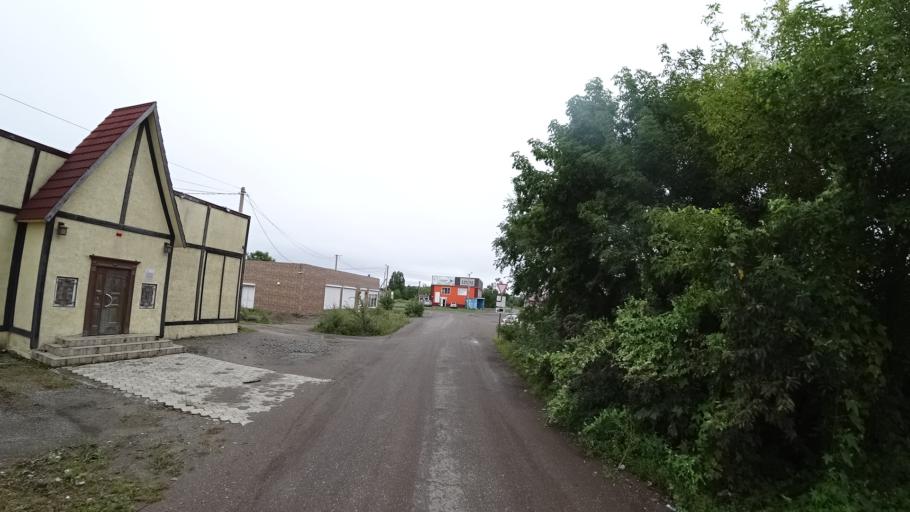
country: RU
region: Primorskiy
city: Monastyrishche
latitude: 44.2065
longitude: 132.4415
